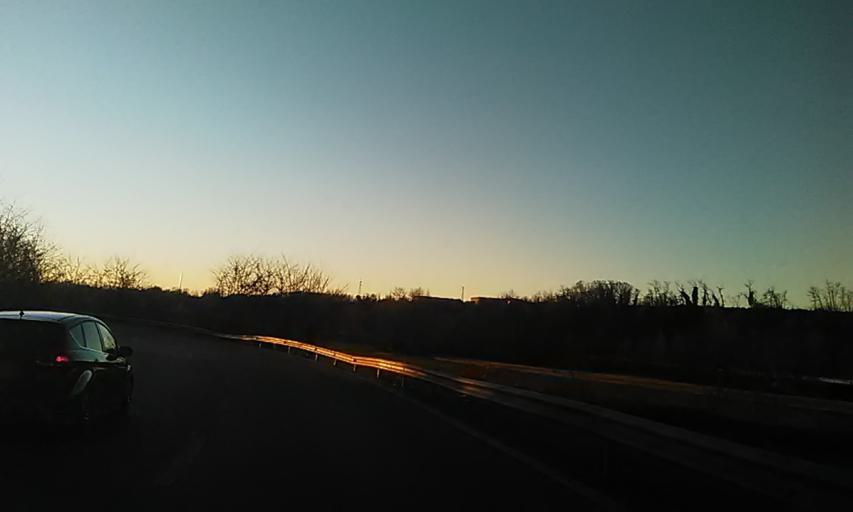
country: IT
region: Piedmont
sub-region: Provincia di Biella
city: Biella
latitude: 45.5609
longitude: 8.0752
